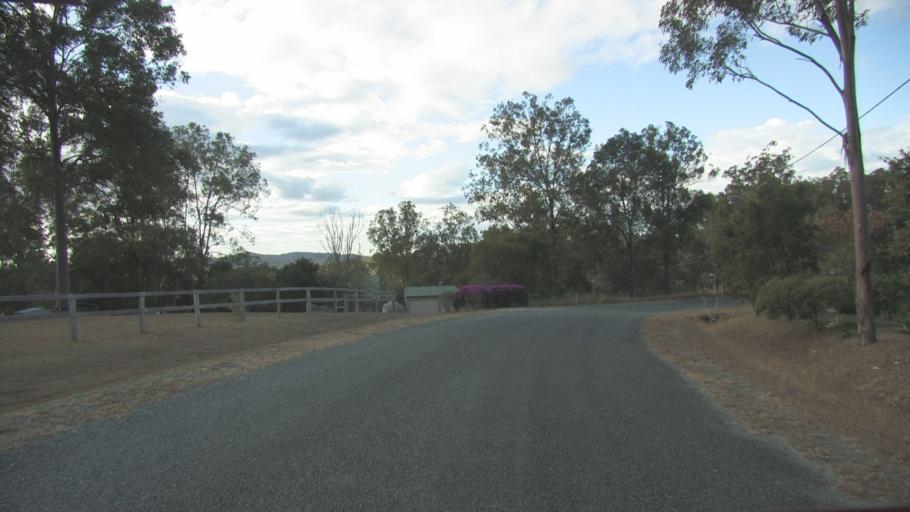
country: AU
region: Queensland
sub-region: Logan
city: Cedar Vale
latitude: -27.8999
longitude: 153.0729
